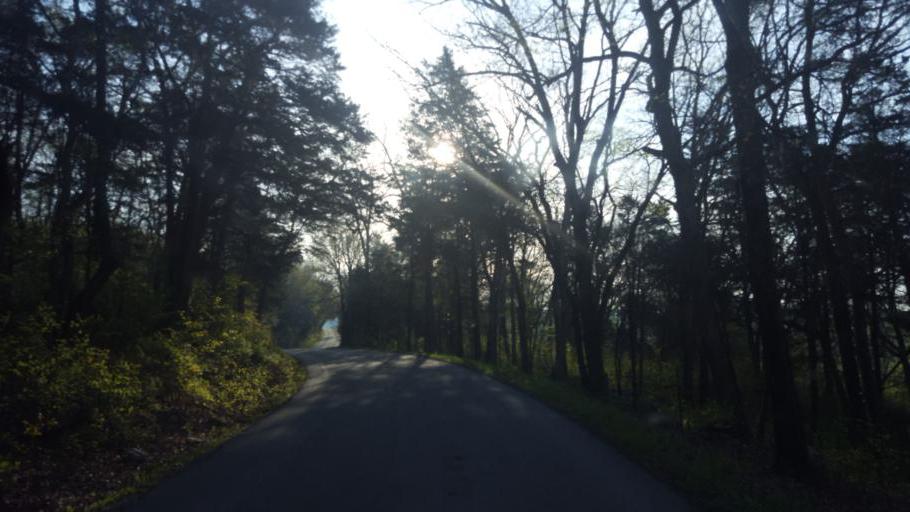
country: US
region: Kentucky
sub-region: Hart County
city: Munfordville
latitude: 37.2444
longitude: -85.9186
